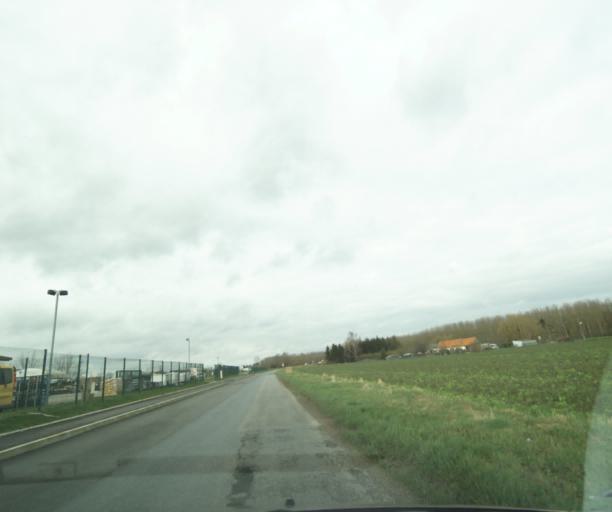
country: FR
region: Picardie
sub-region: Departement de l'Oise
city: Noyon
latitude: 49.5877
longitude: 2.9863
